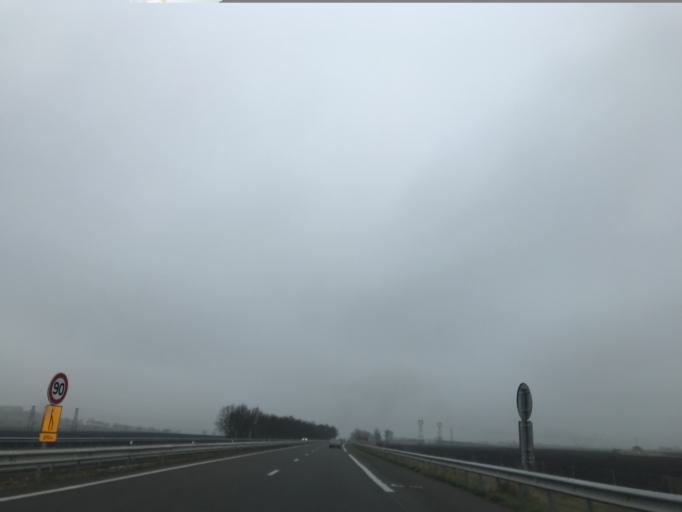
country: FR
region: Auvergne
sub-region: Departement du Puy-de-Dome
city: Pont-du-Chateau
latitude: 45.8155
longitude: 3.2229
